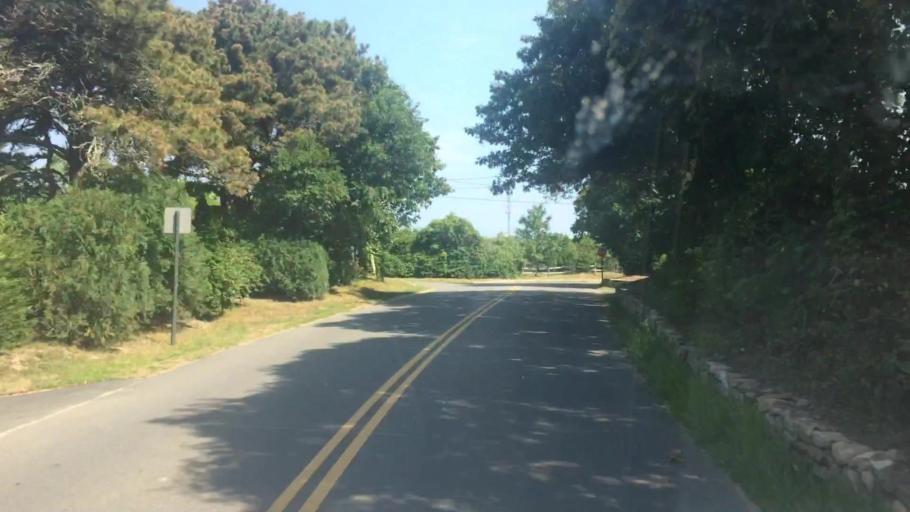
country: US
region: Massachusetts
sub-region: Dukes County
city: Edgartown
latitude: 41.3796
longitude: -70.5275
